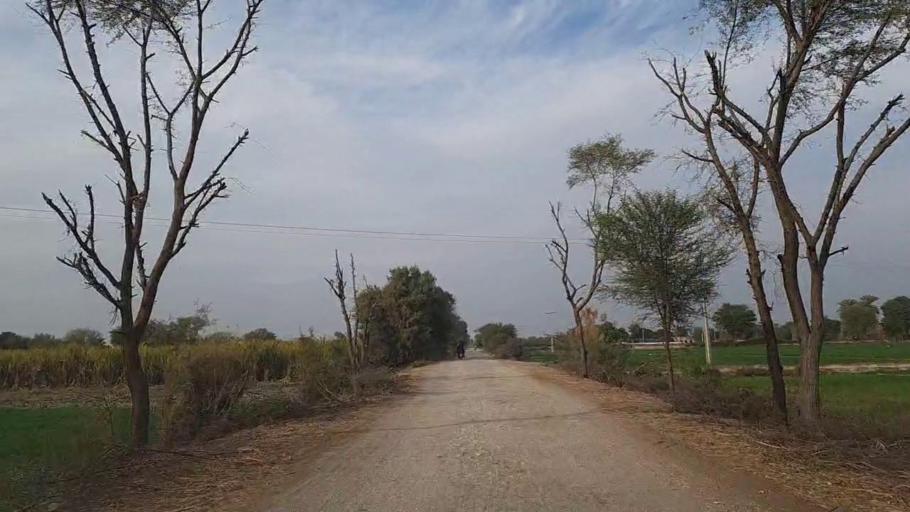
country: PK
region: Sindh
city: Daur
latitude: 26.5206
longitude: 68.4072
